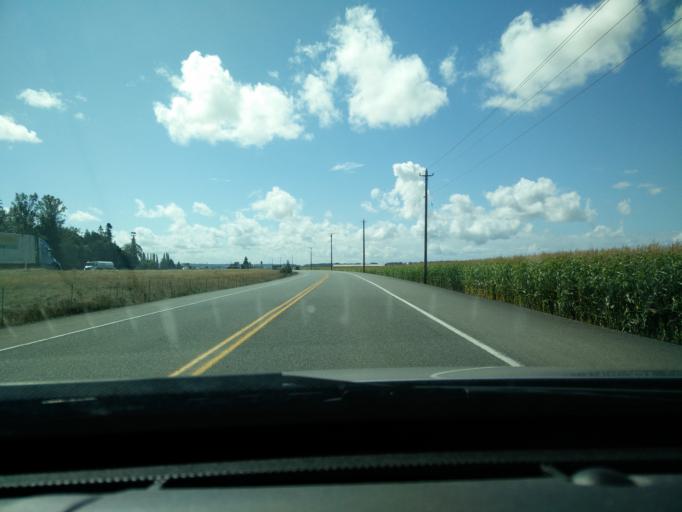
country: US
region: Washington
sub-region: Skagit County
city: Mount Vernon
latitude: 48.3795
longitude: -122.3357
